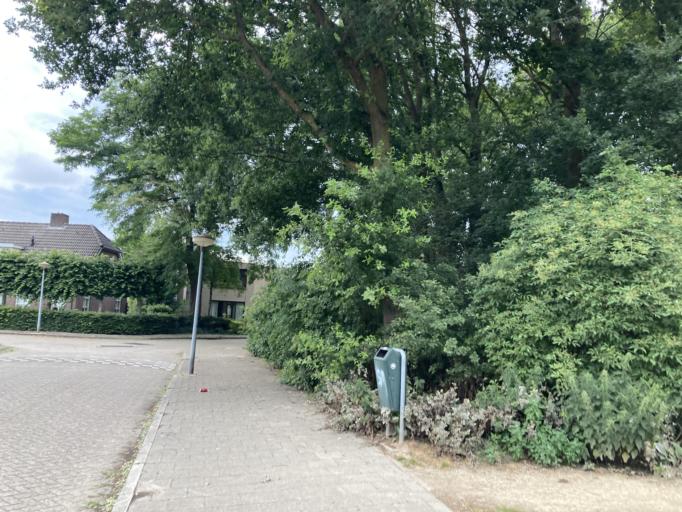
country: NL
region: North Brabant
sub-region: Gemeente Best
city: Best
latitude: 51.4877
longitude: 5.4367
